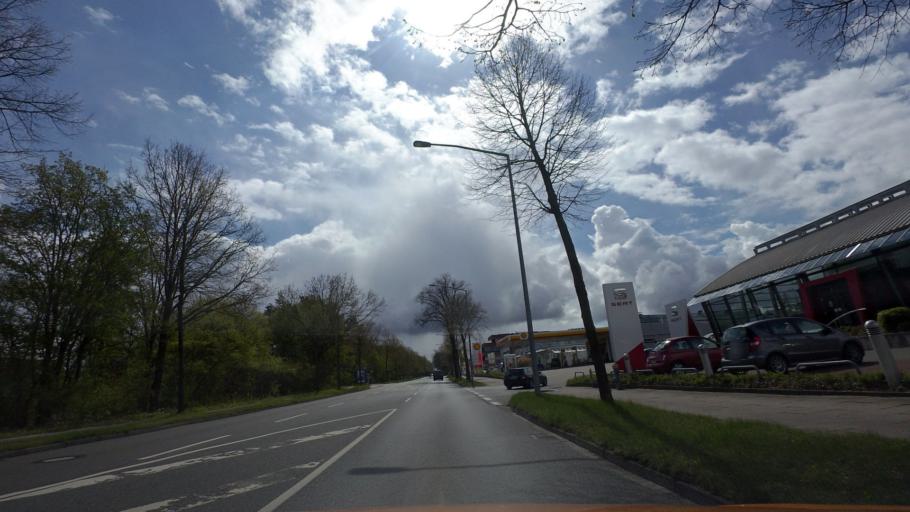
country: DE
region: Lower Saxony
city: Lueneburg
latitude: 53.2252
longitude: 10.4056
